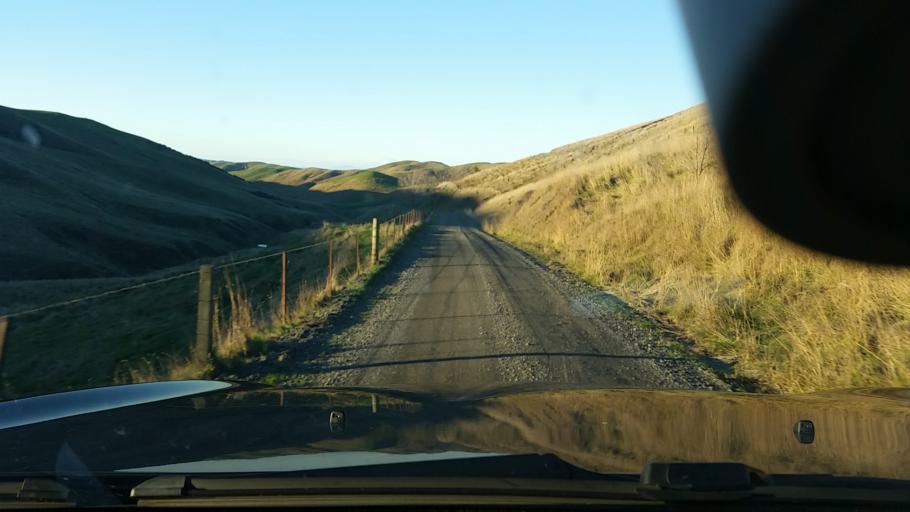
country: NZ
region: Marlborough
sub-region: Marlborough District
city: Blenheim
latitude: -41.7492
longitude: 174.0605
